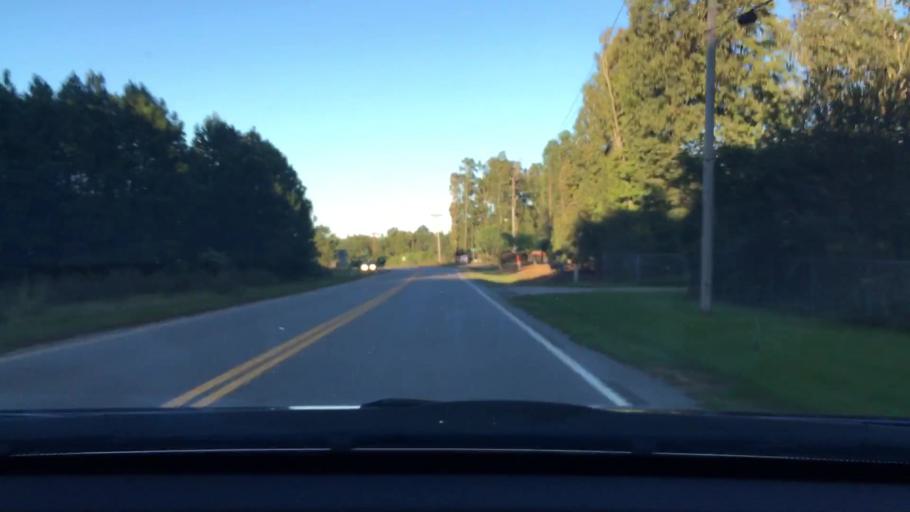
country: US
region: South Carolina
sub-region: Lexington County
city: Irmo
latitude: 34.1243
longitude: -81.1964
